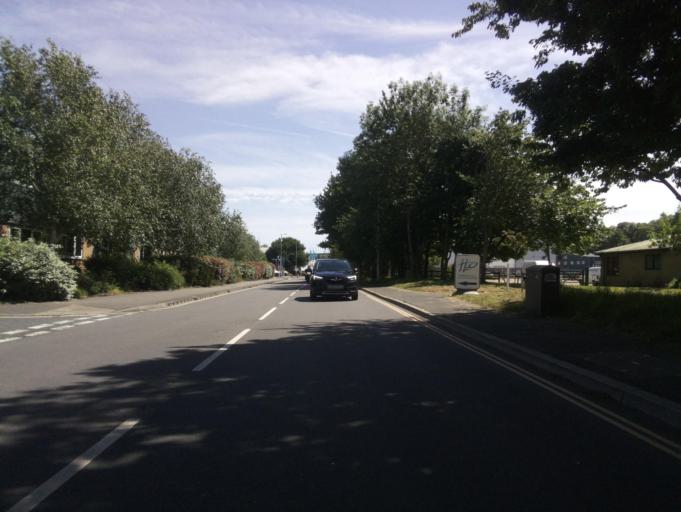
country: GB
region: England
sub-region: Devon
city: Exeter
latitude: 50.6970
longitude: -3.5220
